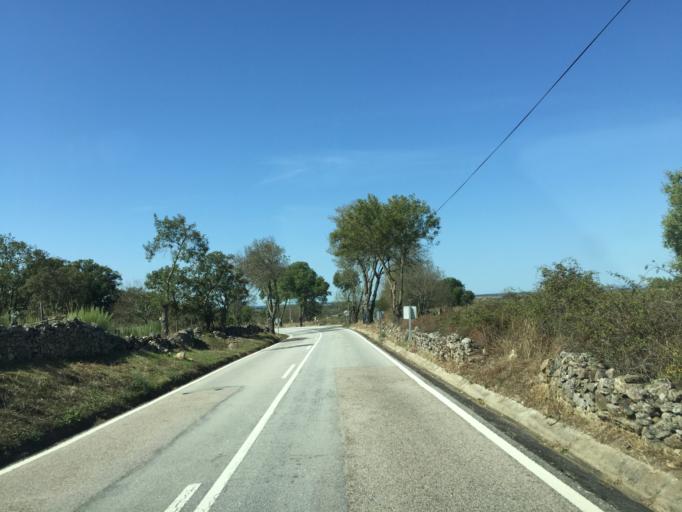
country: PT
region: Portalegre
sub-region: Portalegre
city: Alagoa
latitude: 39.4394
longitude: -7.5603
